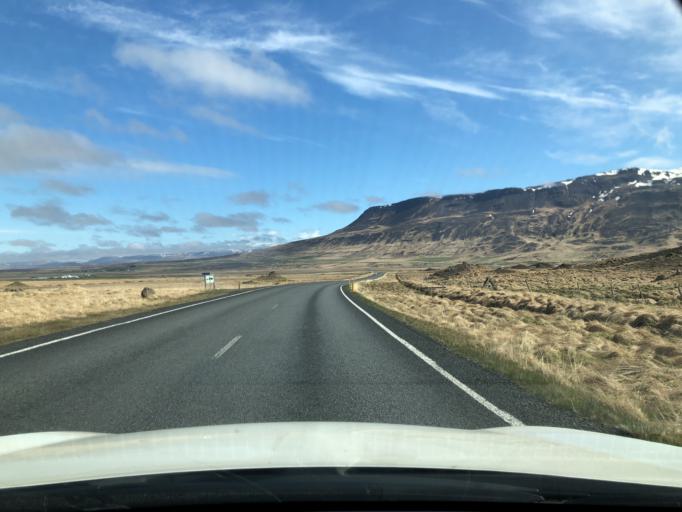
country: IS
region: Northwest
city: Saudarkrokur
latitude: 65.5002
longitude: -20.3998
